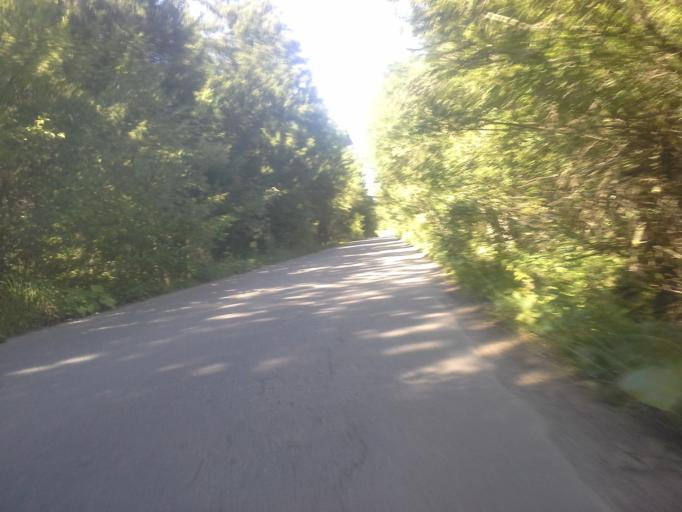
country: RU
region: Moskovskaya
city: Aprelevka
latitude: 55.4637
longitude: 37.0717
